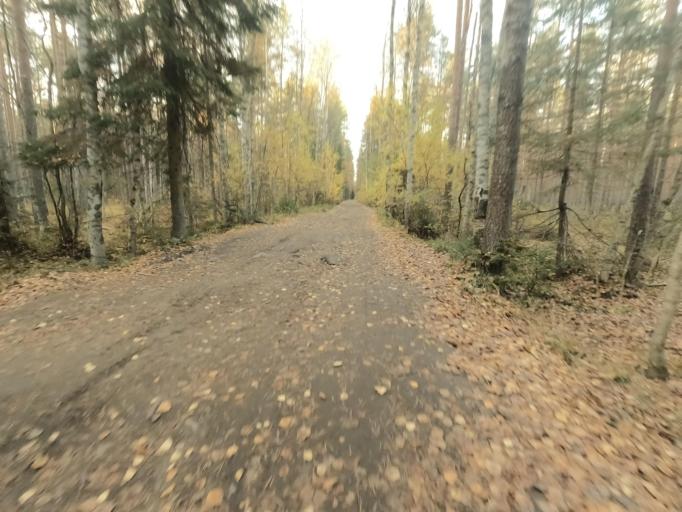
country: RU
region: St.-Petersburg
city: Solnechnoye
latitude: 60.1689
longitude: 29.9644
